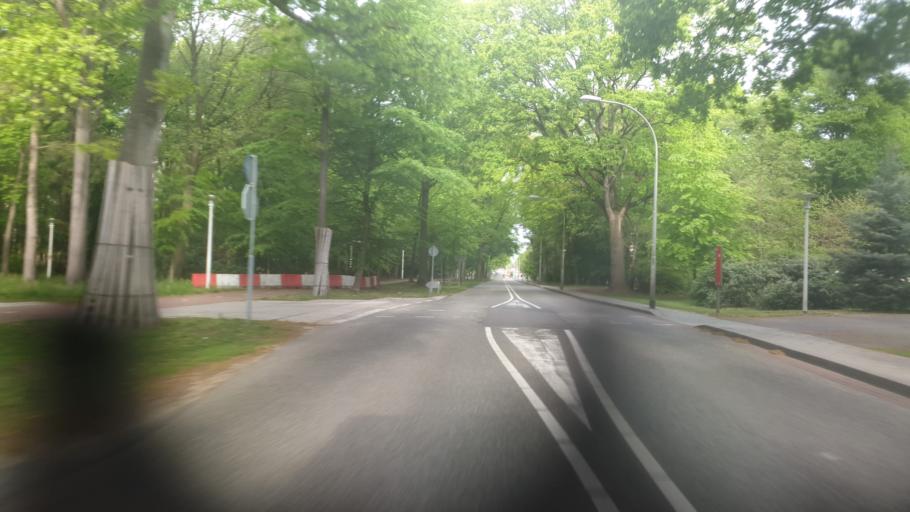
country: NL
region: Gelderland
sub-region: Gemeente Nijmegen
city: Nijmegen
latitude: 51.8204
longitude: 5.8632
